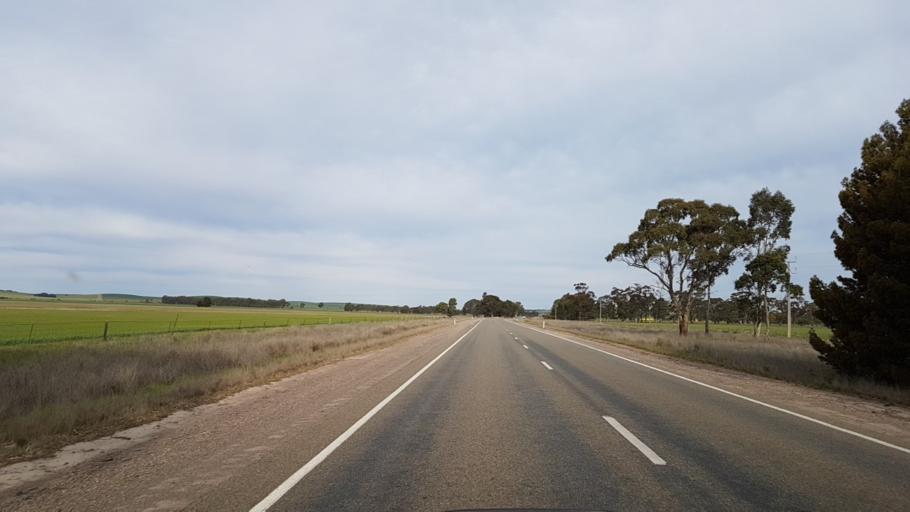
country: AU
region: South Australia
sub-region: Northern Areas
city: Jamestown
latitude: -33.1884
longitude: 138.5064
